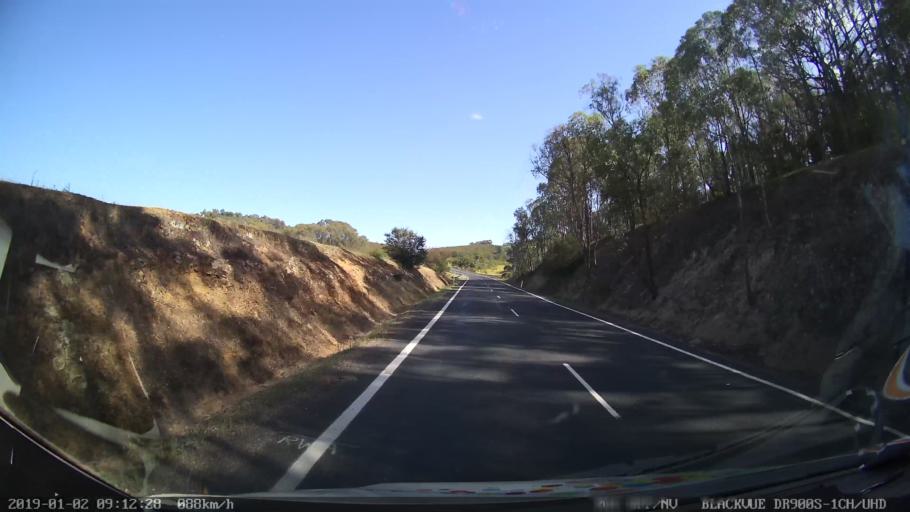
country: AU
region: New South Wales
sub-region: Tumut Shire
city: Tumut
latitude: -35.5000
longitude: 148.2719
